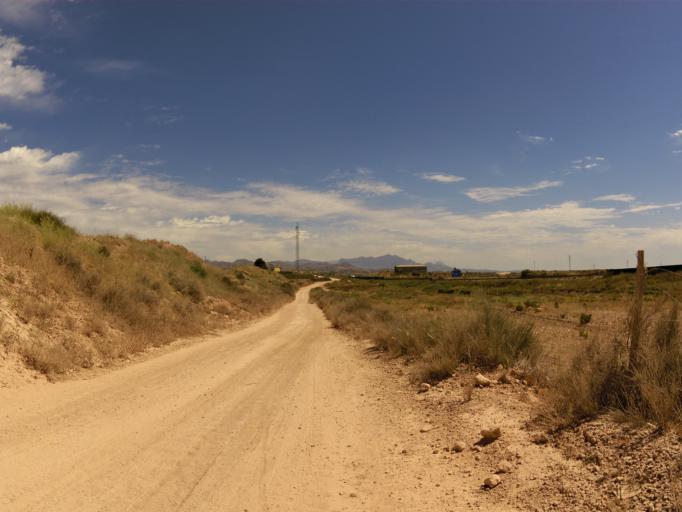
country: ES
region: Valencia
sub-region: Provincia de Alicante
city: Agost
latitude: 38.3988
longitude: -0.6102
